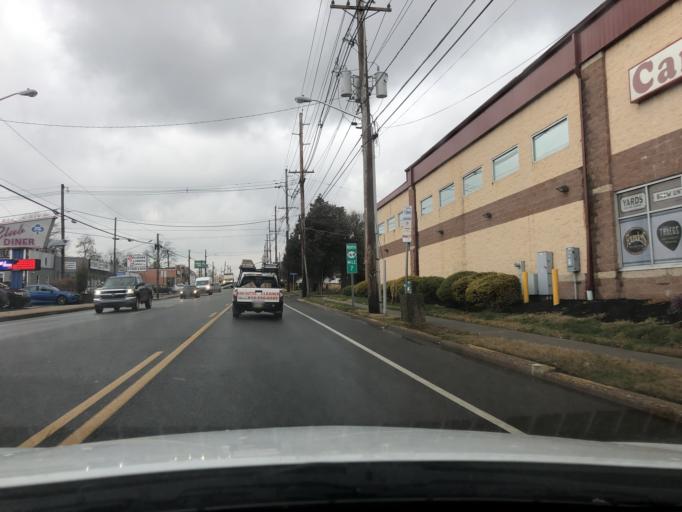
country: US
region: New Jersey
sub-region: Camden County
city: Bellmawr
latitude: 39.8669
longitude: -75.0796
